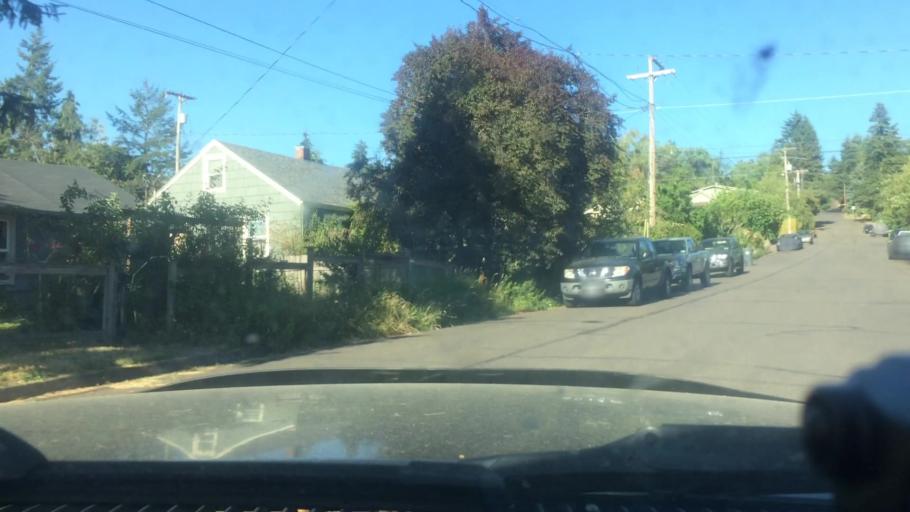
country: US
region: Oregon
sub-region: Lane County
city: Eugene
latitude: 44.0314
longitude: -123.1040
